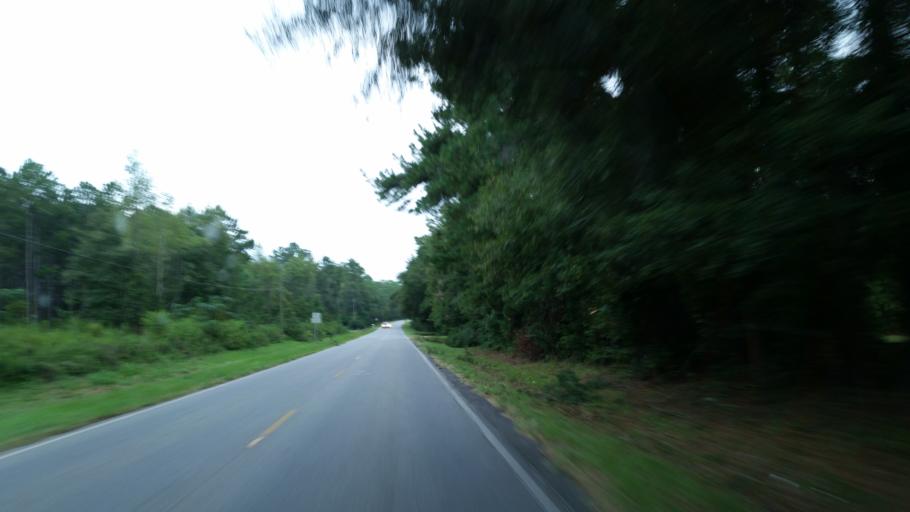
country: US
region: Georgia
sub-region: Lowndes County
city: Valdosta
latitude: 30.7557
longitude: -83.2576
